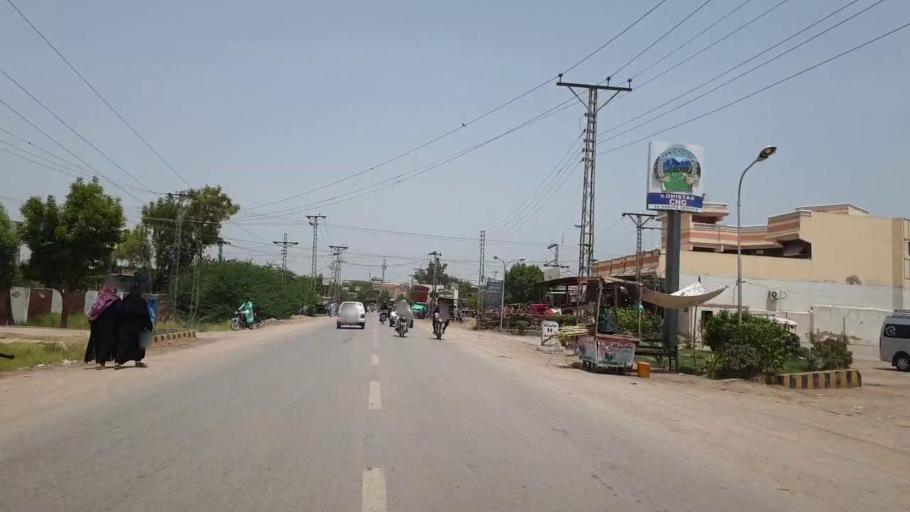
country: PK
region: Sindh
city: Nawabshah
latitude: 26.2508
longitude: 68.4265
